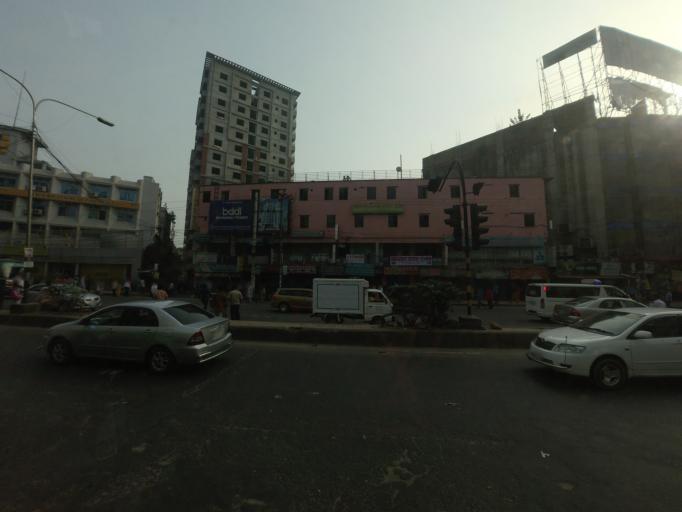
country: BD
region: Dhaka
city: Azimpur
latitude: 23.7750
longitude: 90.3653
